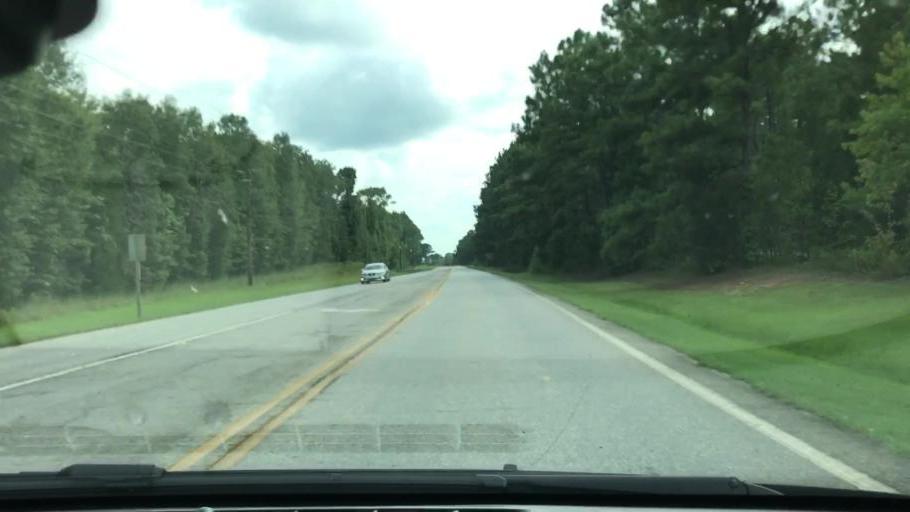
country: US
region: Georgia
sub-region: Clay County
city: Fort Gaines
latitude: 31.6621
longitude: -85.0473
